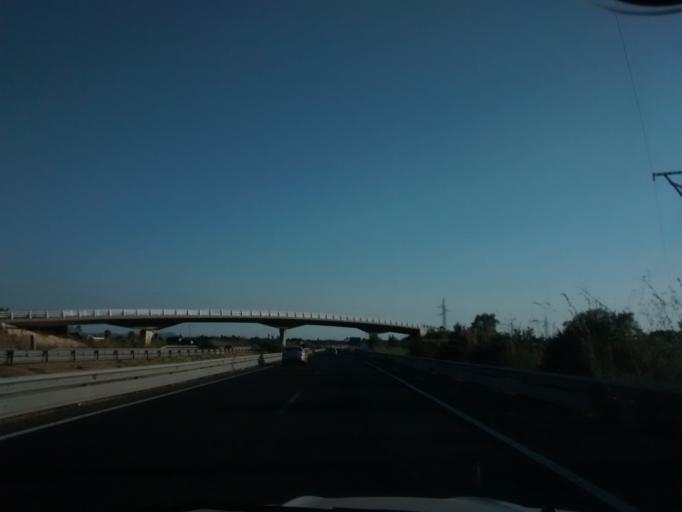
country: ES
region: Balearic Islands
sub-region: Illes Balears
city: Inca
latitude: 39.7231
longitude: 2.9295
